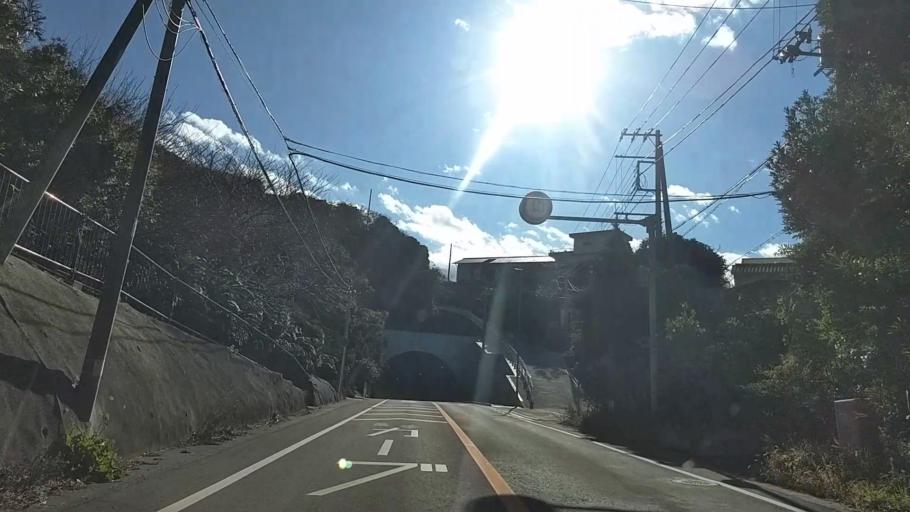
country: JP
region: Chiba
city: Tateyama
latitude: 35.0551
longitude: 139.8295
